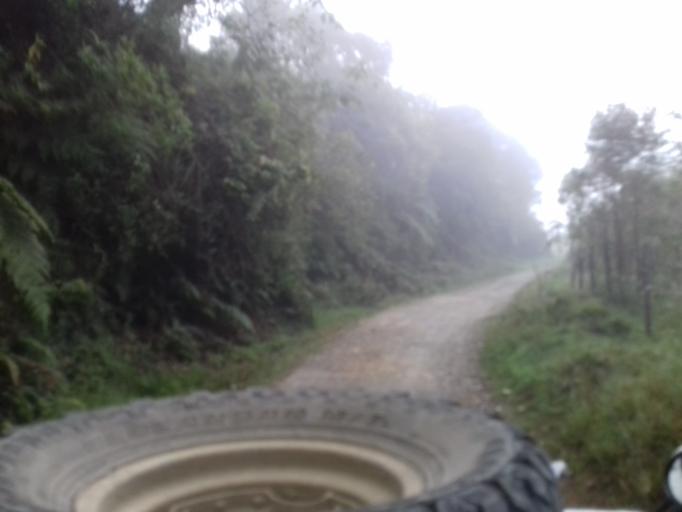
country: CO
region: Quindio
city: Salento
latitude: 4.5547
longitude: -75.5164
